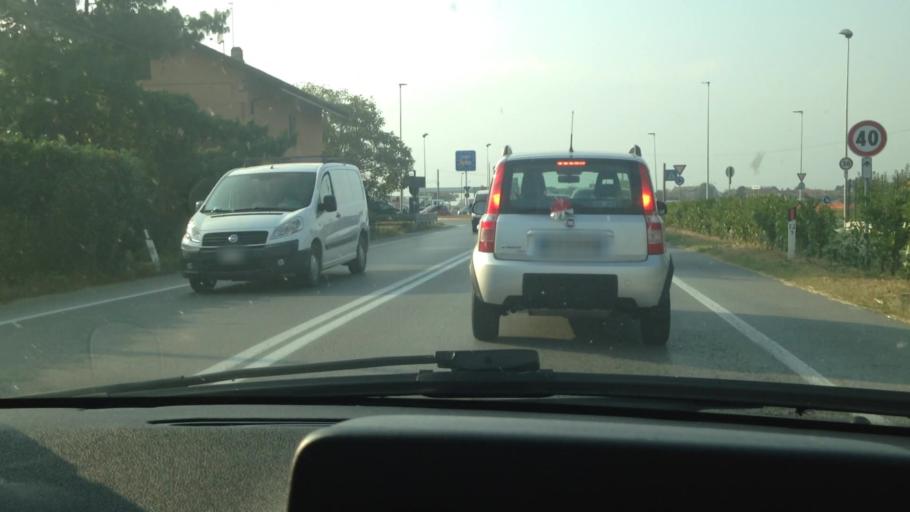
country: IT
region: Piedmont
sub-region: Provincia di Torino
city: San Maurizio
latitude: 45.1935
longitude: 7.6286
